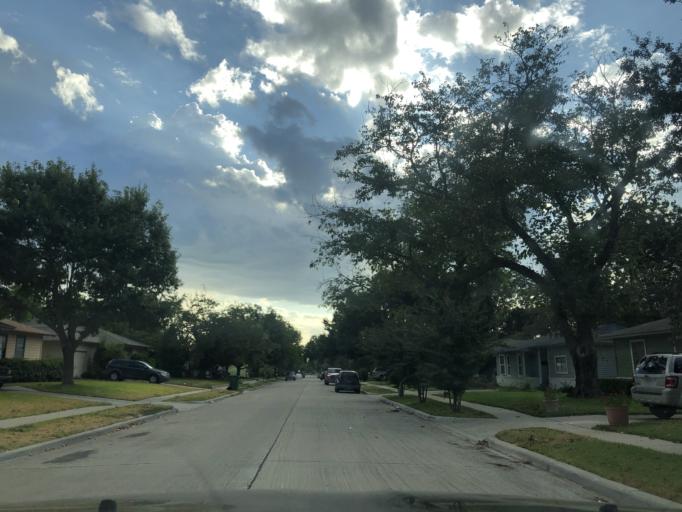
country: US
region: Texas
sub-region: Dallas County
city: Garland
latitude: 32.8753
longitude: -96.6510
